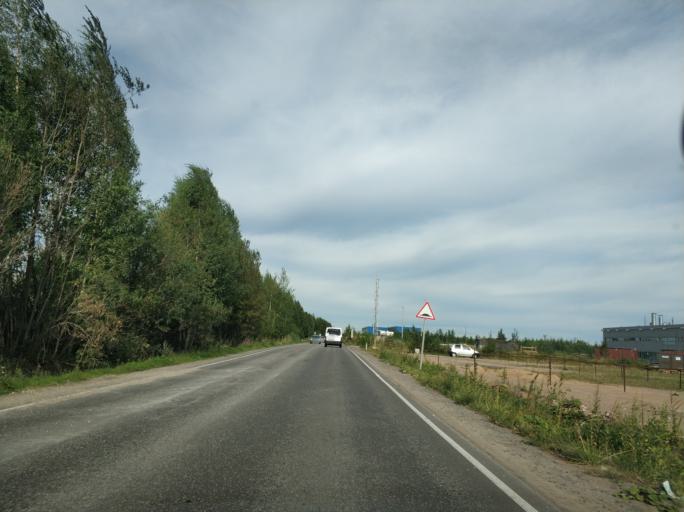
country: RU
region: St.-Petersburg
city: Grazhdanka
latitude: 60.0463
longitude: 30.4184
